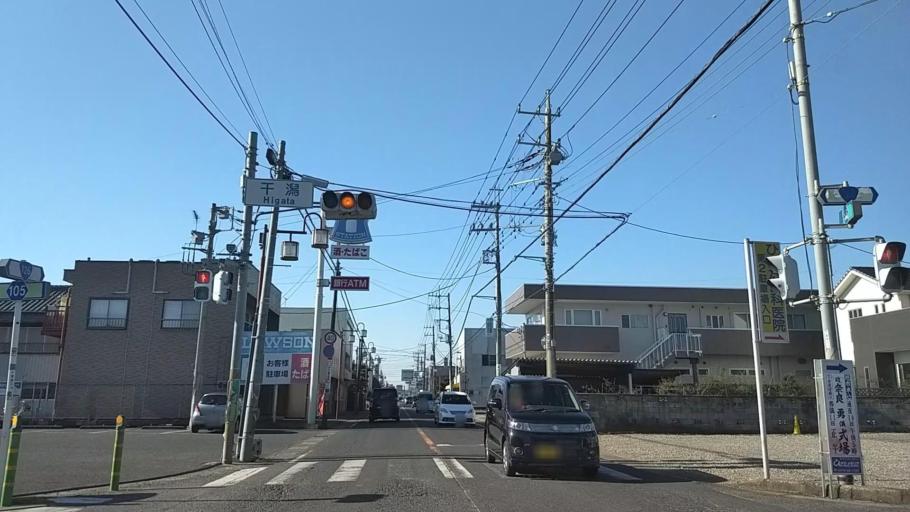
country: JP
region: Chiba
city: Asahi
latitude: 35.7180
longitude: 140.6001
